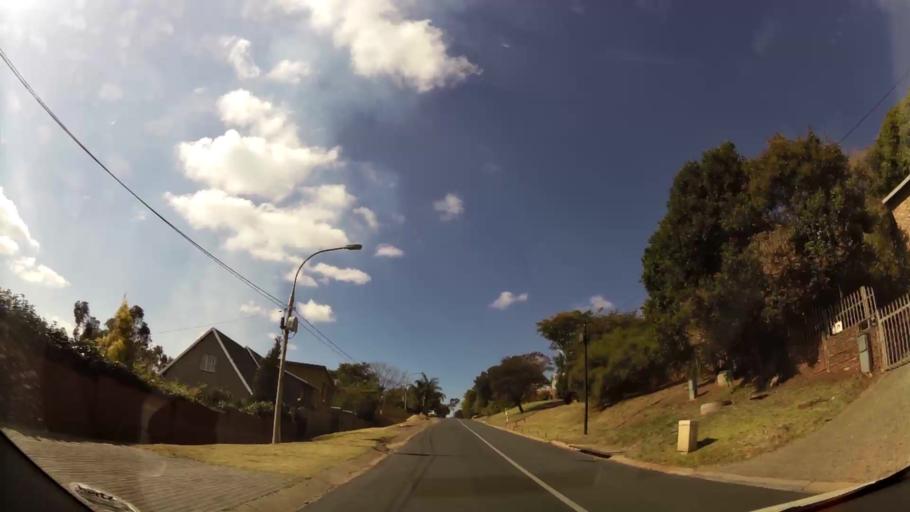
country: ZA
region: Gauteng
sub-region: City of Johannesburg Metropolitan Municipality
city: Roodepoort
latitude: -26.1133
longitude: 27.8412
